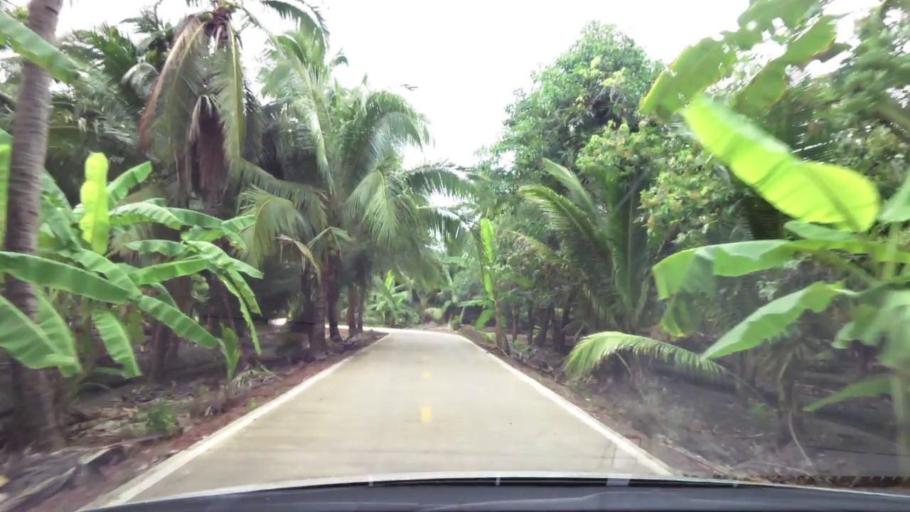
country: TH
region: Ratchaburi
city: Damnoen Saduak
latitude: 13.5492
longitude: 99.9899
